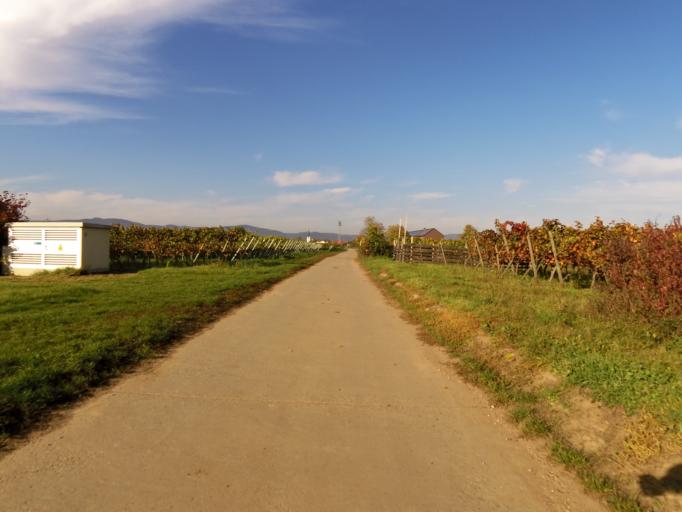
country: DE
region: Rheinland-Pfalz
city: Gonnheim
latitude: 49.4459
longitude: 8.2341
